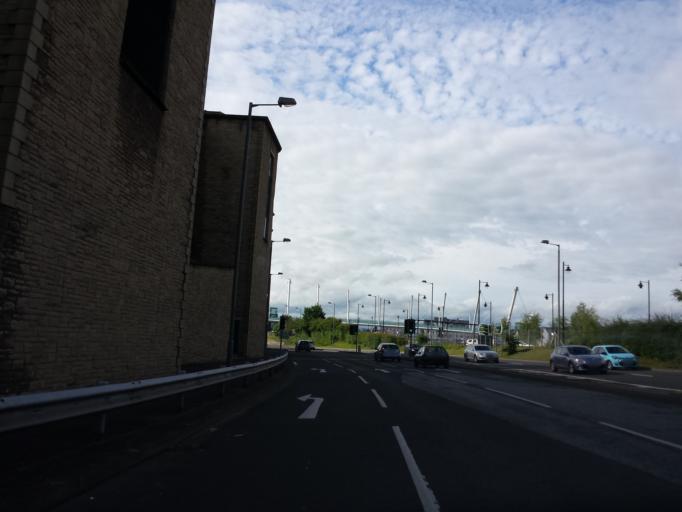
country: GB
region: Scotland
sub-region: Stirling
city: Stirling
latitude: 56.1171
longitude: -3.9327
